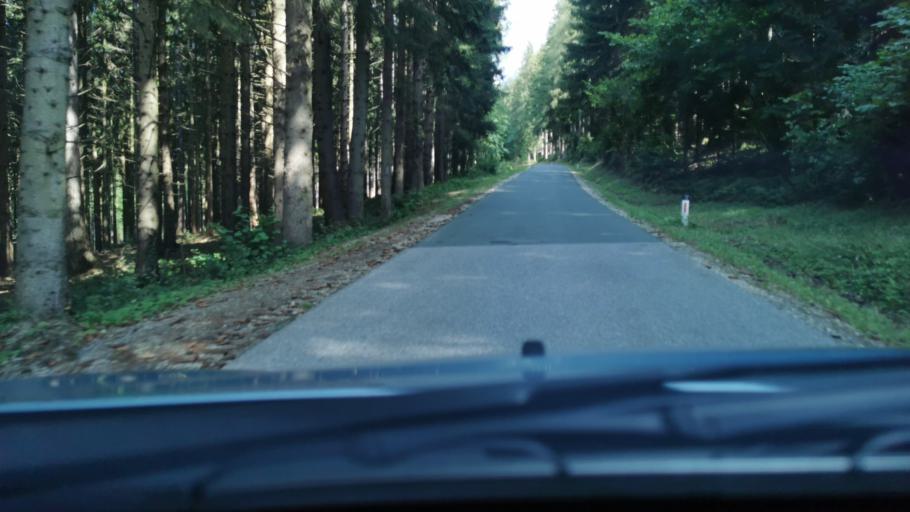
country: AT
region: Styria
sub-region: Politischer Bezirk Weiz
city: Baierdorf-Umgebung
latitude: 47.3056
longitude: 15.7060
